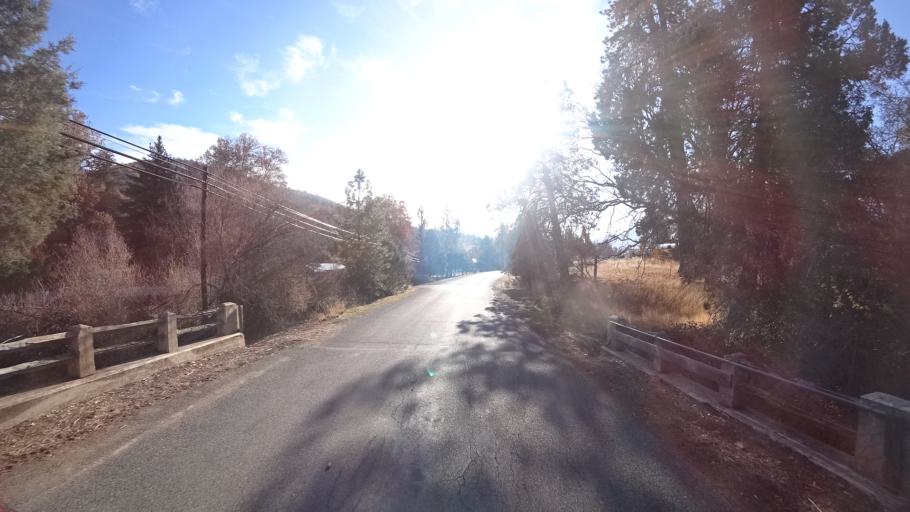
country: US
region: California
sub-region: Siskiyou County
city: Yreka
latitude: 41.6861
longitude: -122.6329
